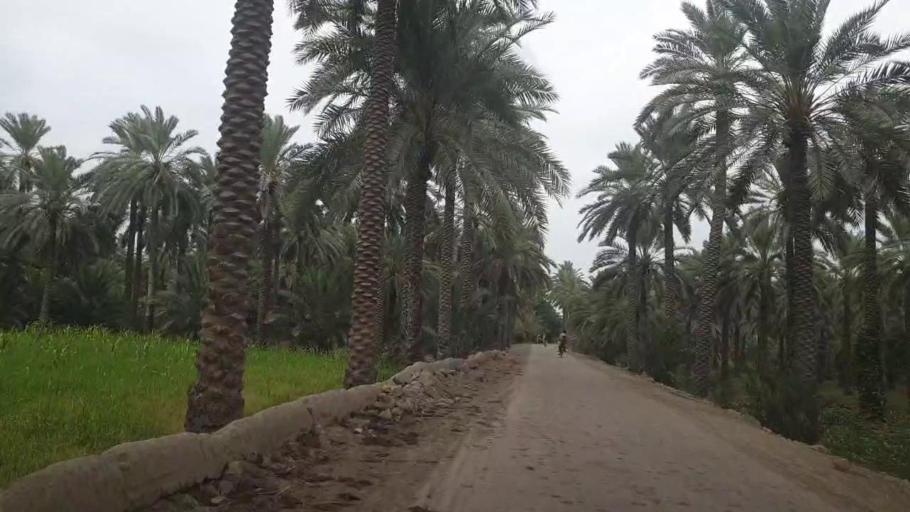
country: PK
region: Sindh
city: Khairpur
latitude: 27.5722
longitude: 68.7420
